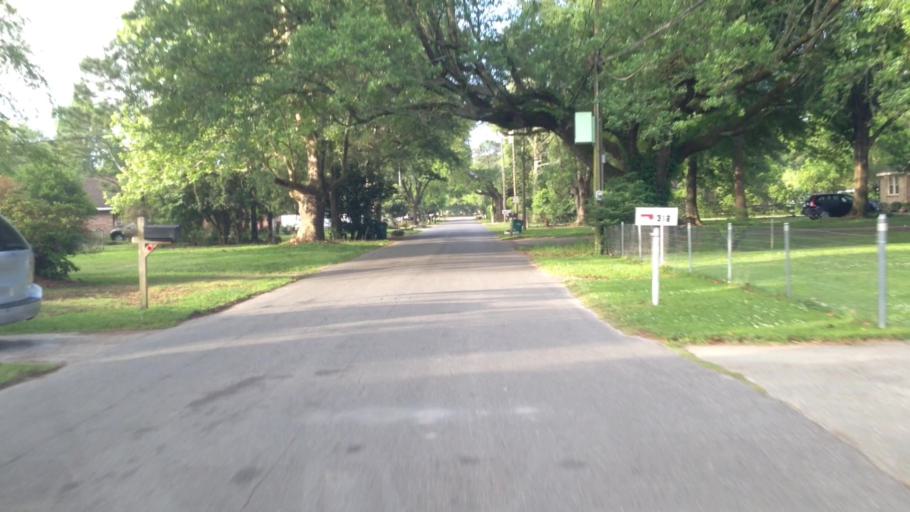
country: US
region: Louisiana
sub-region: Jefferson Parish
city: Jefferson
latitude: 29.9476
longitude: -90.1519
